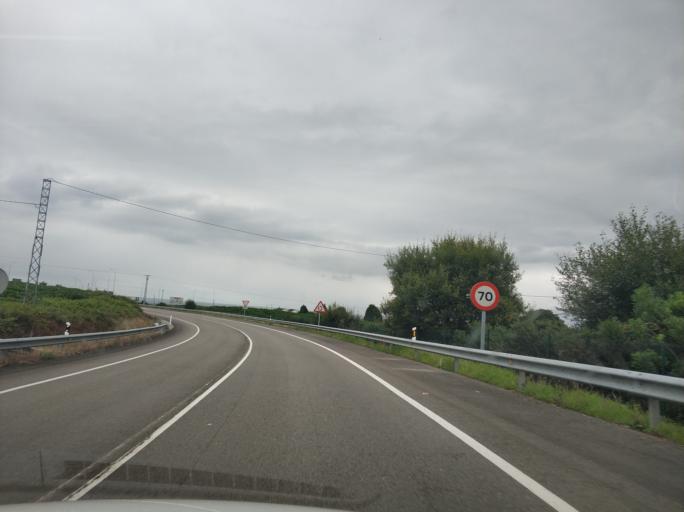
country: ES
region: Galicia
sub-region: Provincia de Lugo
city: Barreiros
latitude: 43.5448
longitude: -7.1515
